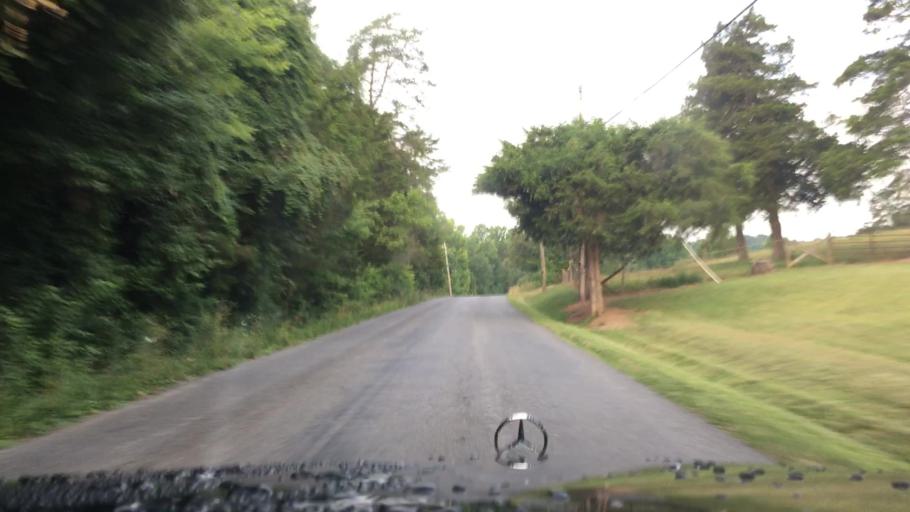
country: US
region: Virginia
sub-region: Campbell County
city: Altavista
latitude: 37.1462
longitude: -79.2818
